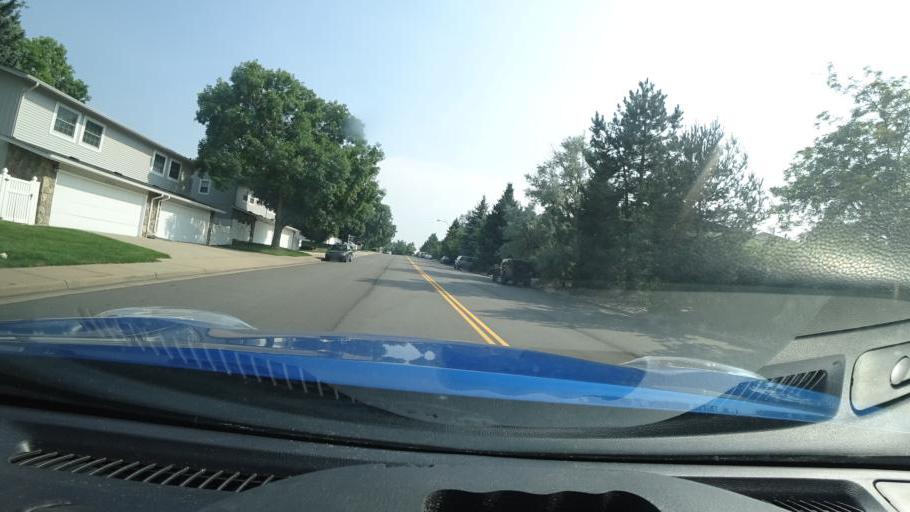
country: US
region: Colorado
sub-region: Adams County
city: Aurora
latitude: 39.6656
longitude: -104.8356
